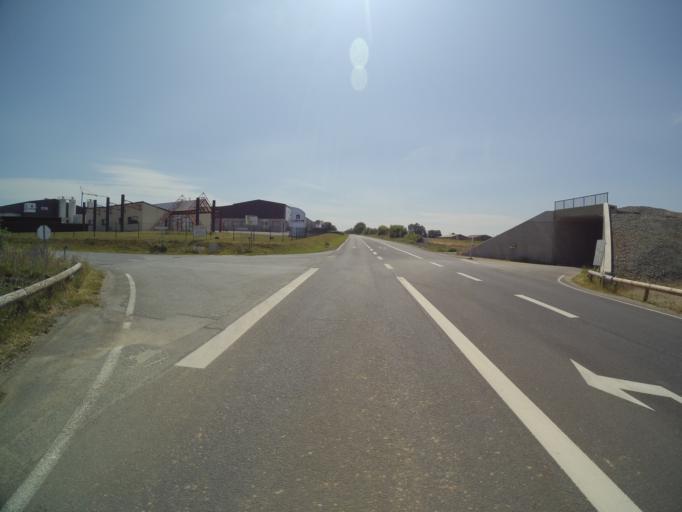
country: FR
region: Pays de la Loire
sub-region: Departement de la Vendee
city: Saint-Michel-Mont-Mercure
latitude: 46.8180
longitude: -0.8713
